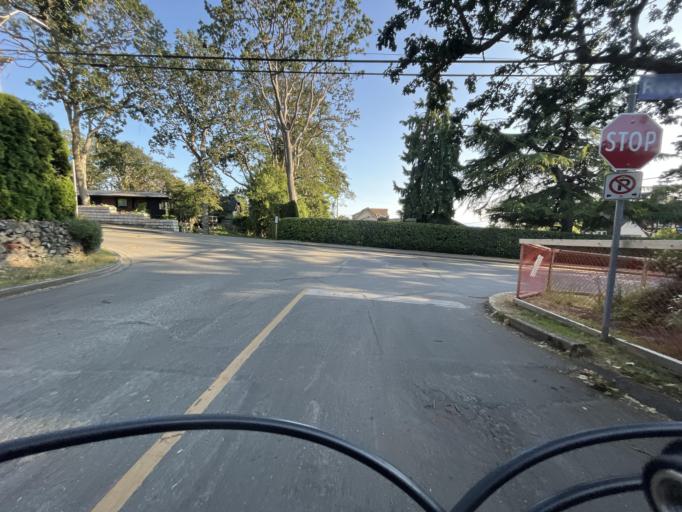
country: CA
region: British Columbia
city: Victoria
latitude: 48.4199
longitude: -123.3447
